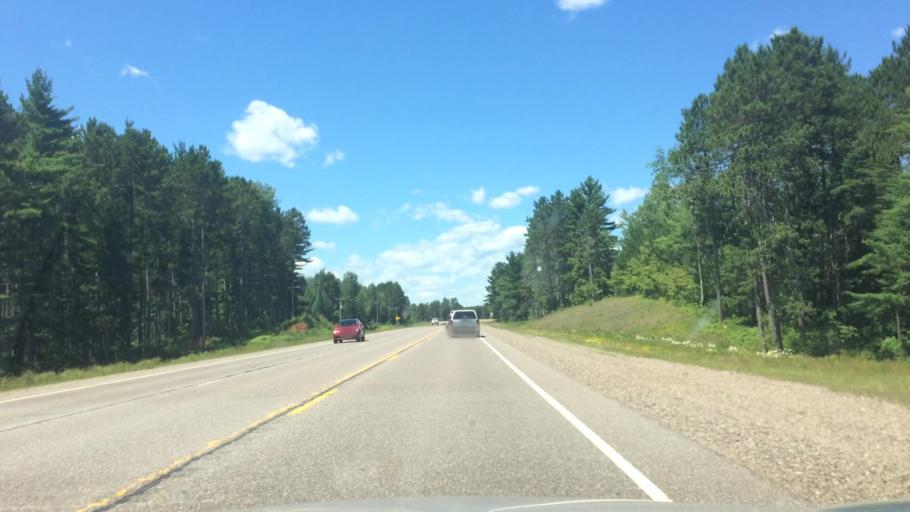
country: US
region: Wisconsin
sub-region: Lincoln County
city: Tomahawk
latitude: 45.6600
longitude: -89.7084
